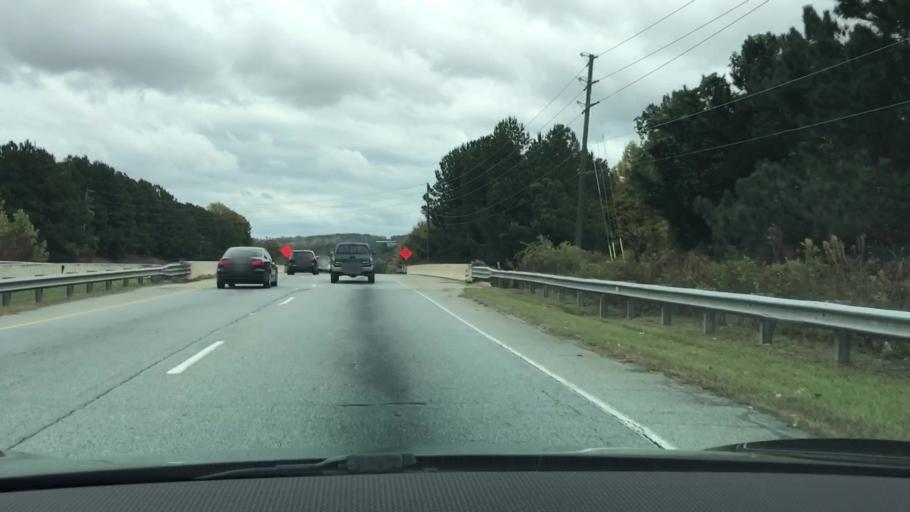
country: US
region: Georgia
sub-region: Gwinnett County
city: Suwanee
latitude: 34.0441
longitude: -84.0834
